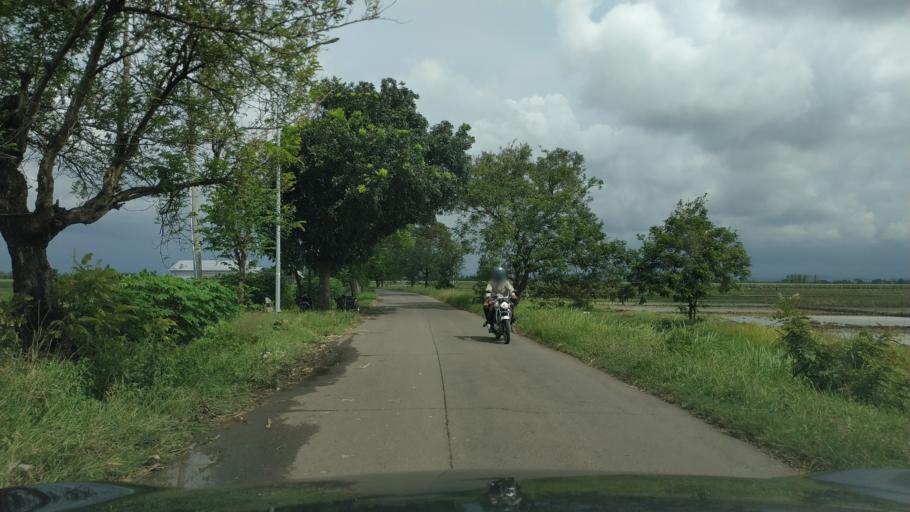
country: ID
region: Central Java
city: Pemalang
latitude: -6.8999
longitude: 109.3251
